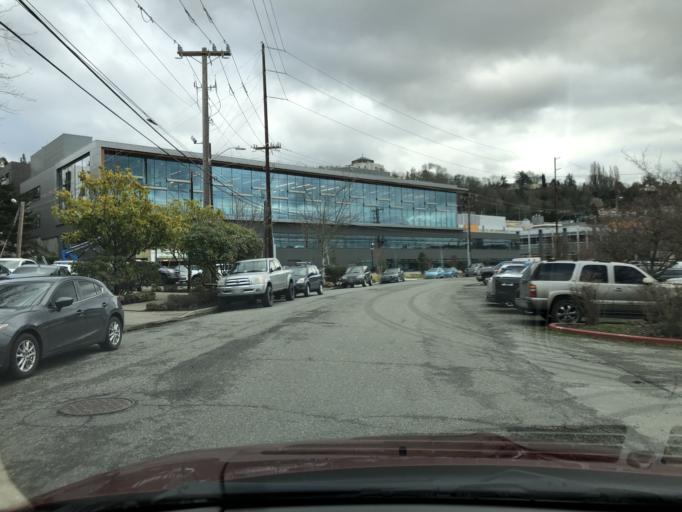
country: US
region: Washington
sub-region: King County
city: Seattle
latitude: 47.6360
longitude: -122.3276
